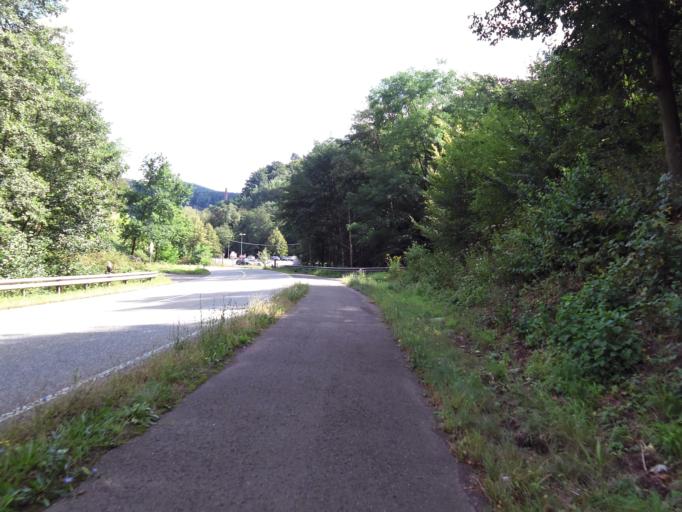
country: DE
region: Rheinland-Pfalz
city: Neidenfels
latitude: 49.3911
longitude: 8.0395
